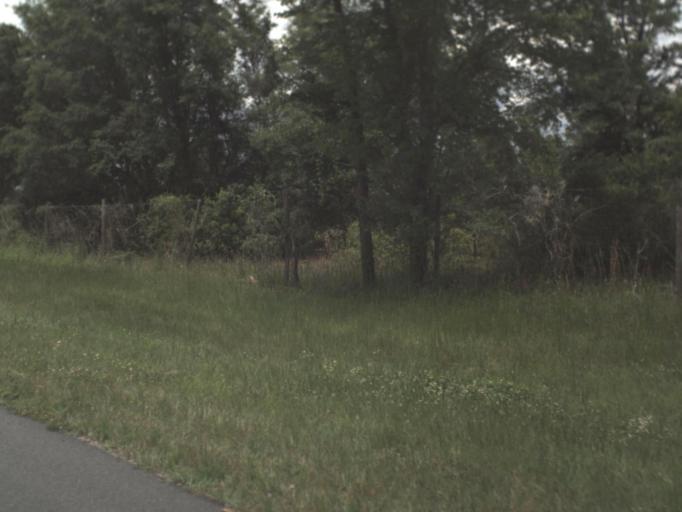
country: US
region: Florida
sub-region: Hamilton County
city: Jasper
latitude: 30.5146
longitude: -82.6703
